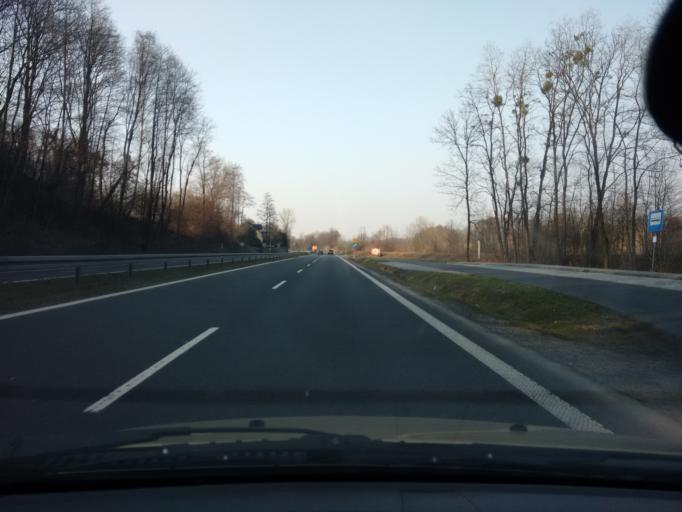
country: PL
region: Silesian Voivodeship
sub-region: Powiat cieszynski
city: Ochaby
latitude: 49.8272
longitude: 18.7875
